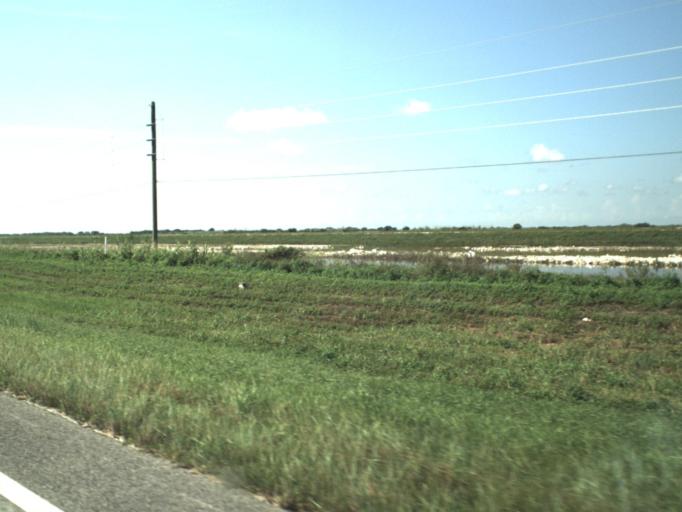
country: US
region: Florida
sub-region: Palm Beach County
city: Belle Glade Camp
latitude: 26.4474
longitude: -80.6251
